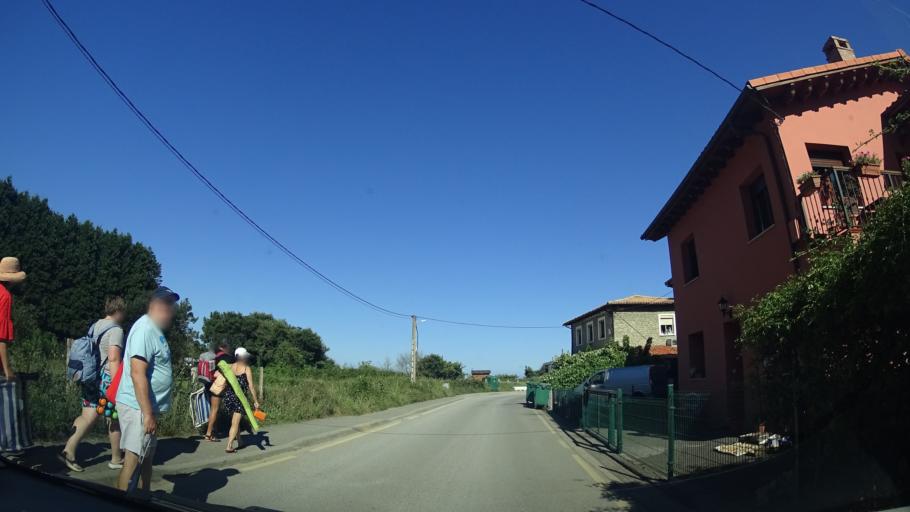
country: ES
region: Asturias
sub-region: Province of Asturias
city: Ribadesella
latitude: 43.4791
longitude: -5.1339
